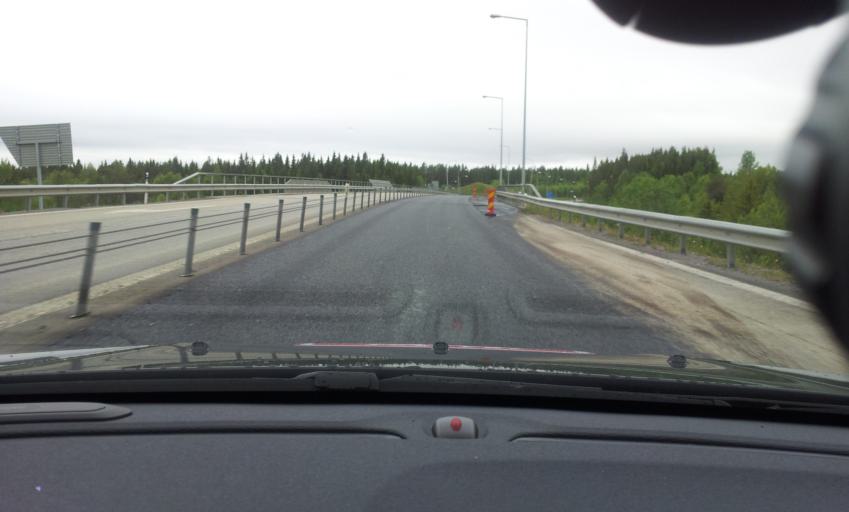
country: SE
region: Jaemtland
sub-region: OEstersunds Kommun
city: Ostersund
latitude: 63.2146
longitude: 14.6437
